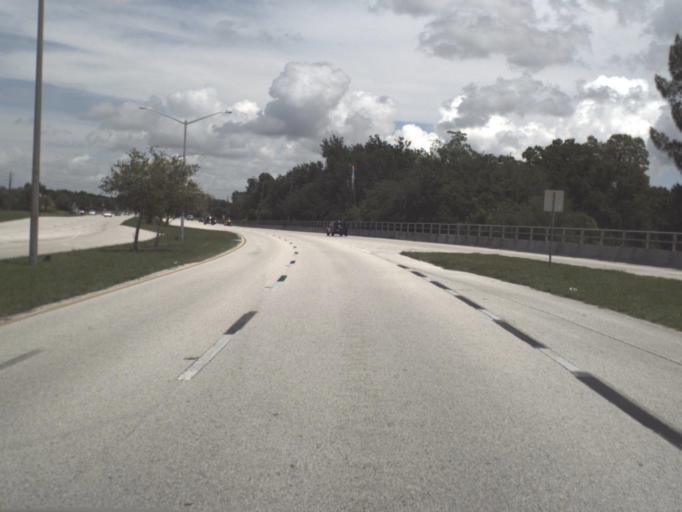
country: US
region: Florida
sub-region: Pinellas County
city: Saint George
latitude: 28.0684
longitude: -82.7053
